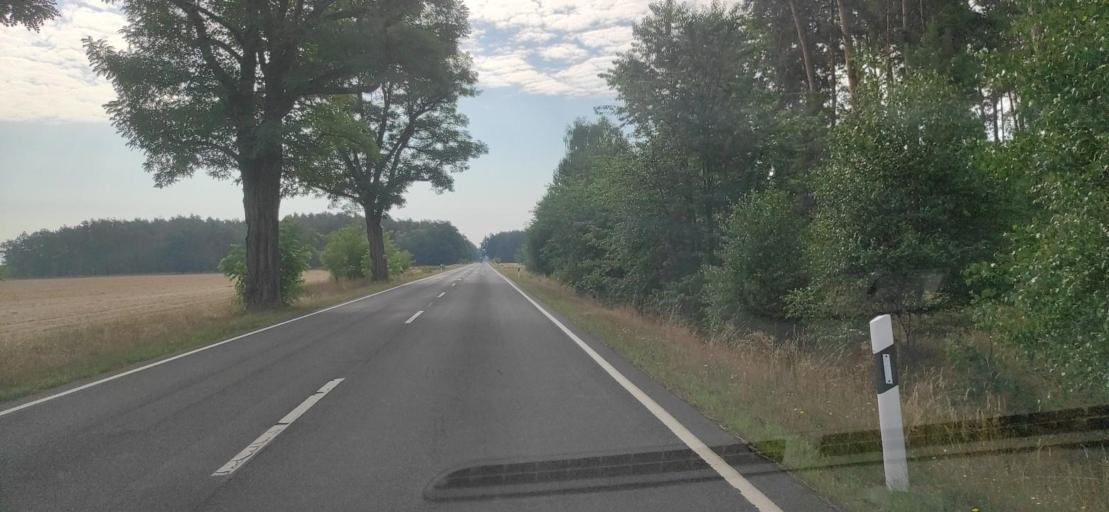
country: DE
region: Brandenburg
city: Forst
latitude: 51.7028
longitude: 14.6895
